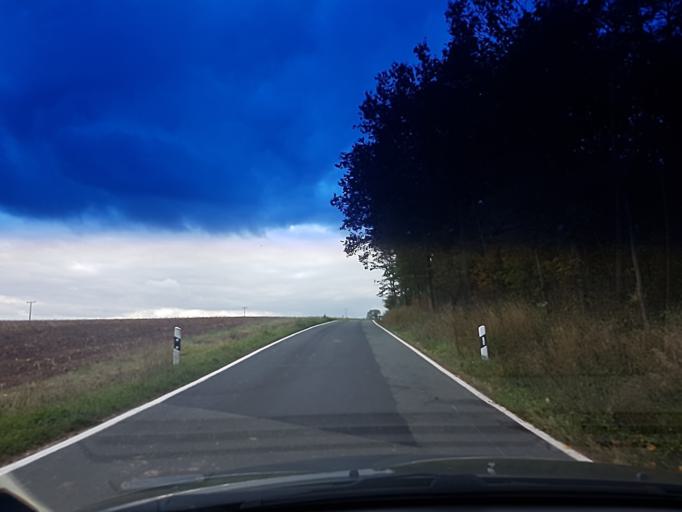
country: DE
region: Bavaria
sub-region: Regierungsbezirk Mittelfranken
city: Hochstadt an der Aisch
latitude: 49.7286
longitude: 10.8364
